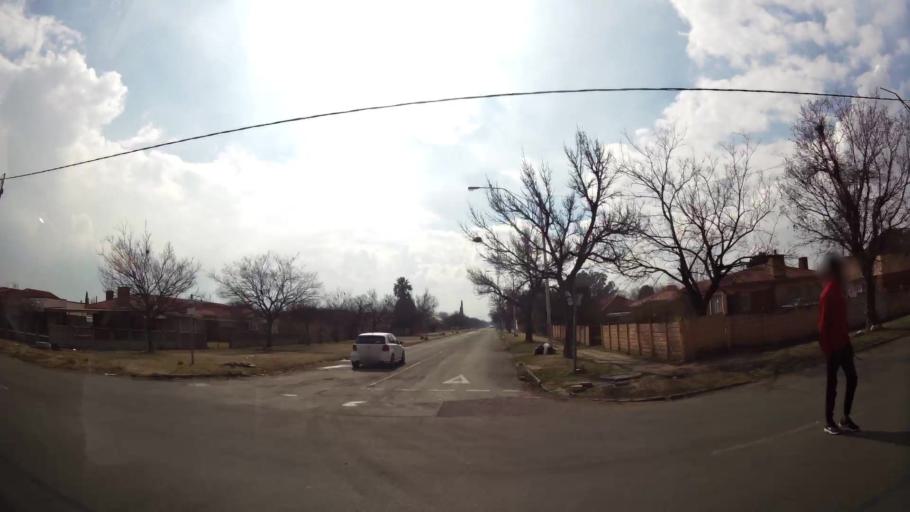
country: ZA
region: Gauteng
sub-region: Sedibeng District Municipality
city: Vereeniging
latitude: -26.6828
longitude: 27.9209
